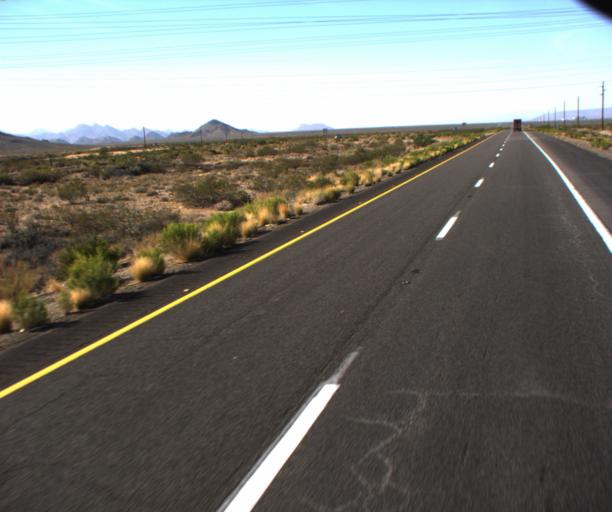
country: US
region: Arizona
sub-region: Mohave County
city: Kingman
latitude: 35.1062
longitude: -114.1172
